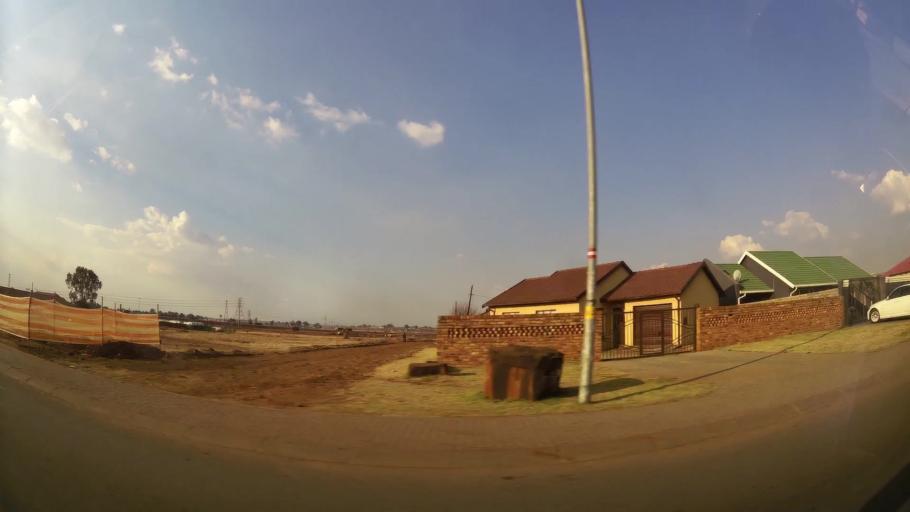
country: ZA
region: Gauteng
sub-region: Ekurhuleni Metropolitan Municipality
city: Germiston
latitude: -26.3466
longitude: 28.2182
